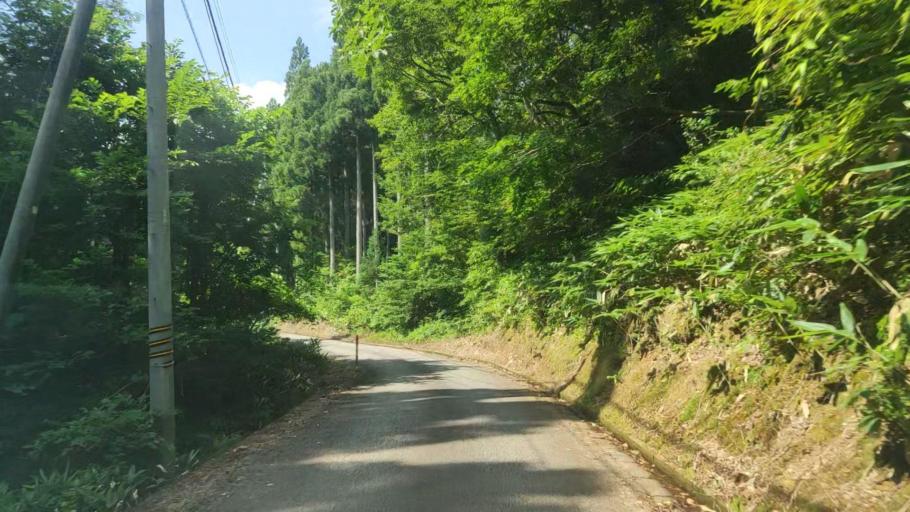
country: JP
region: Ishikawa
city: Komatsu
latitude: 36.2680
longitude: 136.5340
